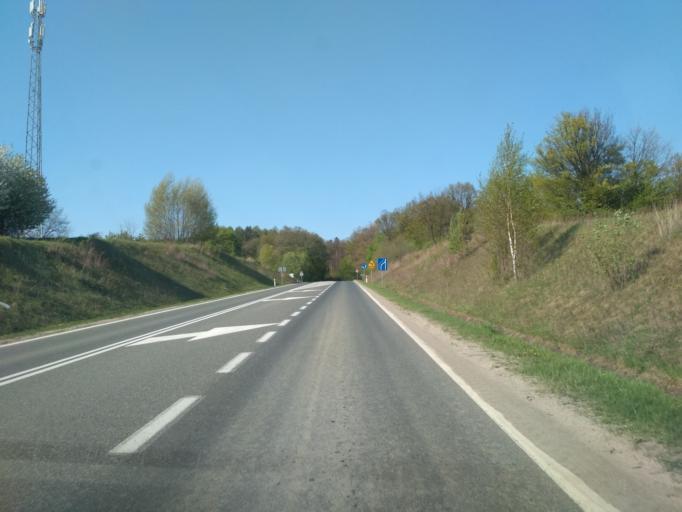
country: PL
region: Subcarpathian Voivodeship
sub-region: Powiat jasielski
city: Tarnowiec
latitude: 49.7727
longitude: 21.5496
